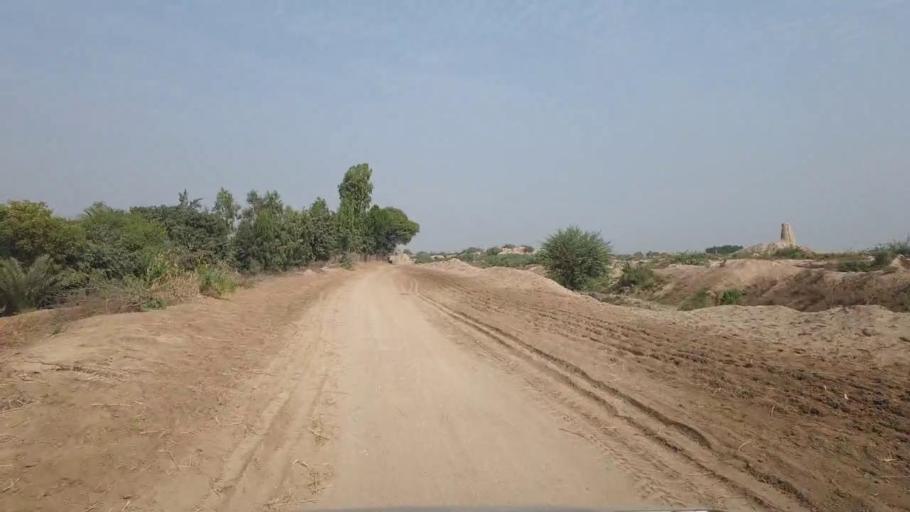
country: PK
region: Sindh
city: Tando Muhammad Khan
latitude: 25.1590
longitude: 68.4690
